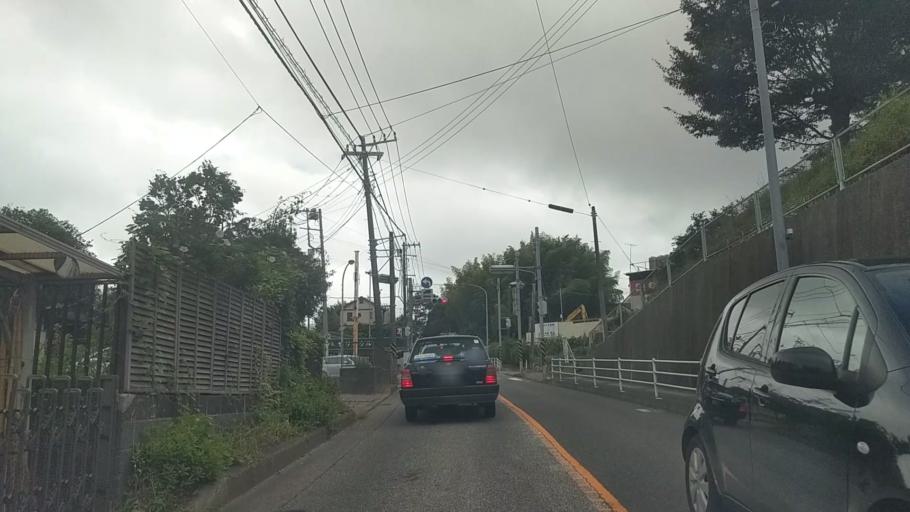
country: JP
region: Kanagawa
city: Yokosuka
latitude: 35.2312
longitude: 139.6488
